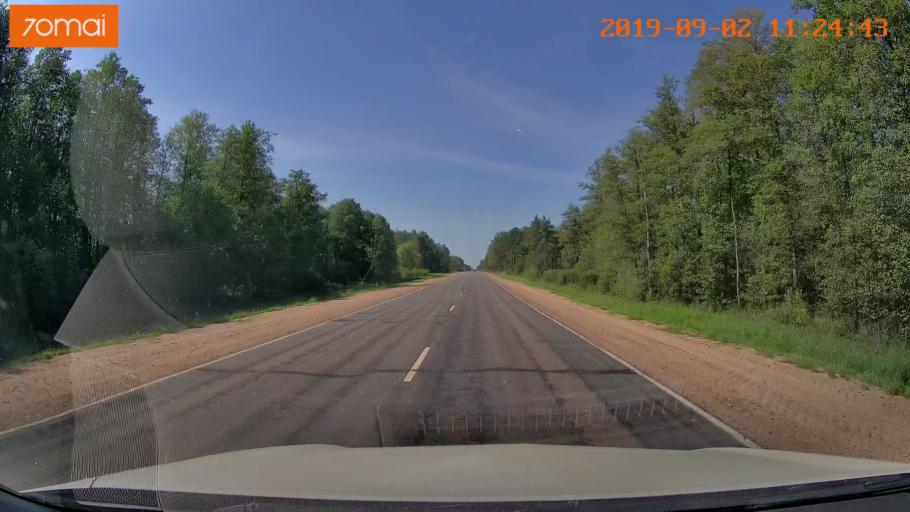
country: RU
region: Smolensk
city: Roslavl'
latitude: 54.0080
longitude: 32.9694
